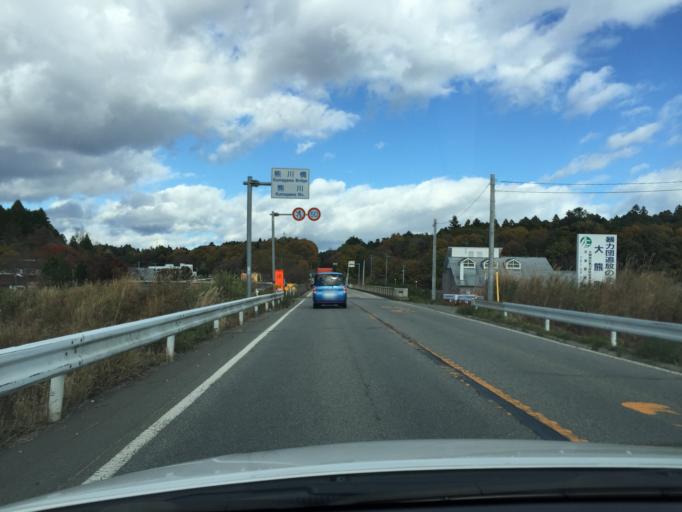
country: JP
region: Fukushima
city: Namie
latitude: 37.3881
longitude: 141.0082
